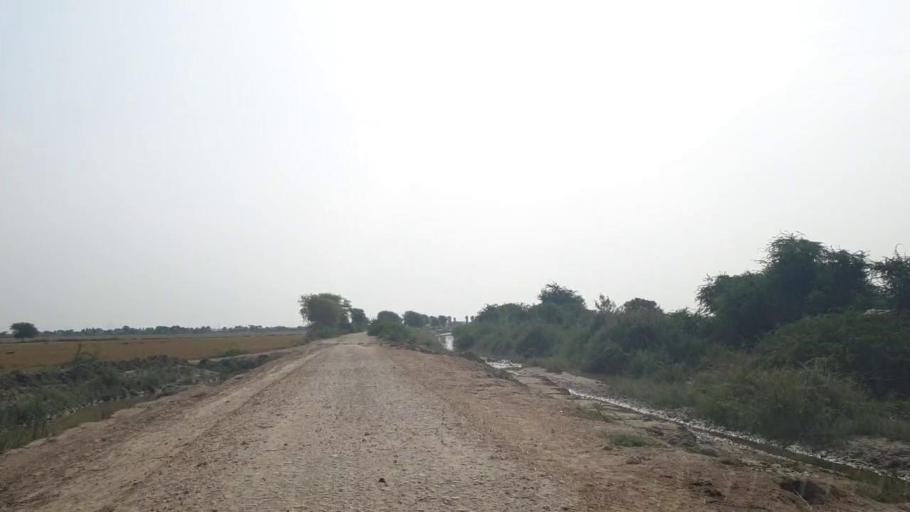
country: PK
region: Sindh
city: Badin
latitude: 24.7599
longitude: 68.7587
